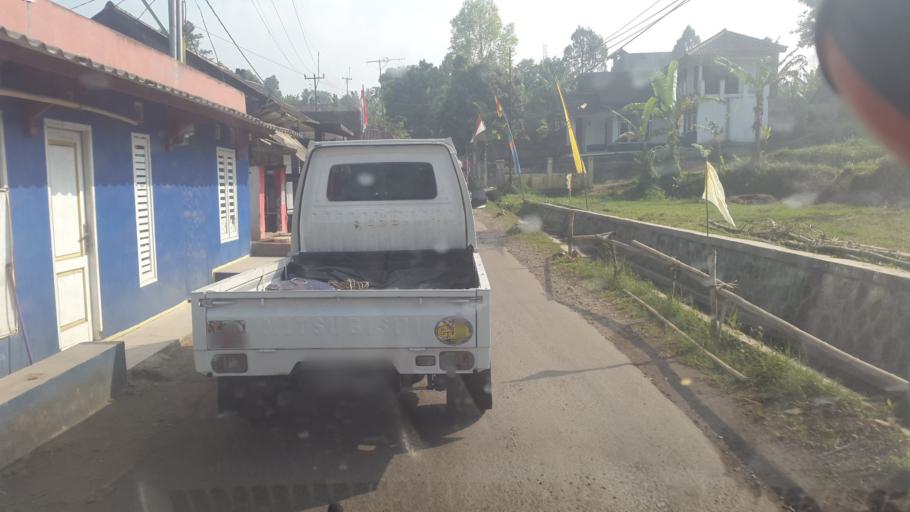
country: ID
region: West Java
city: Sukabumi
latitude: -6.9077
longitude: 106.9773
